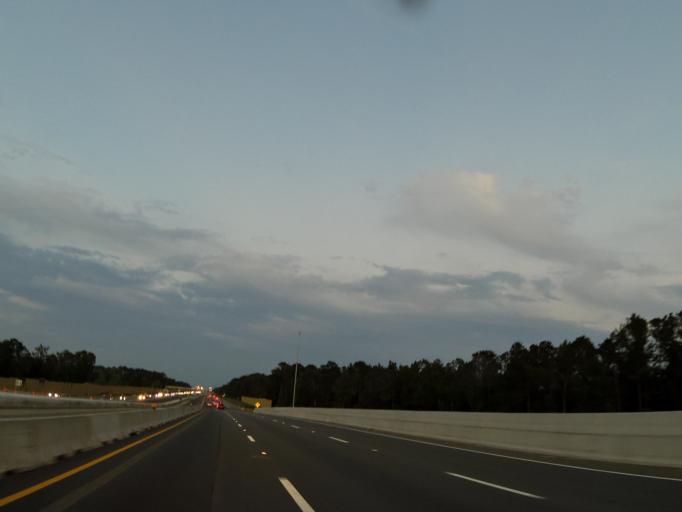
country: US
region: Florida
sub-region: Saint Johns County
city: Fruit Cove
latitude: 30.1689
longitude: -81.6011
